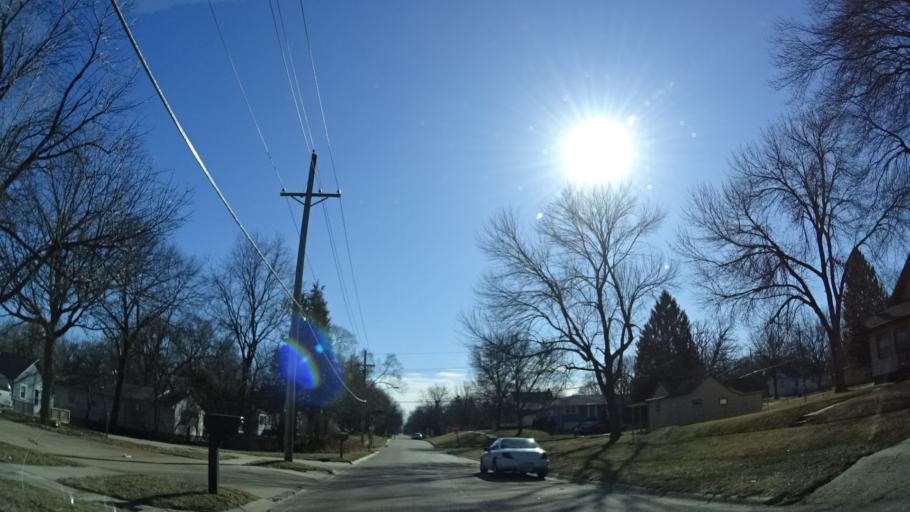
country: US
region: Nebraska
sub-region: Sarpy County
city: Bellevue
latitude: 41.1444
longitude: -95.8909
